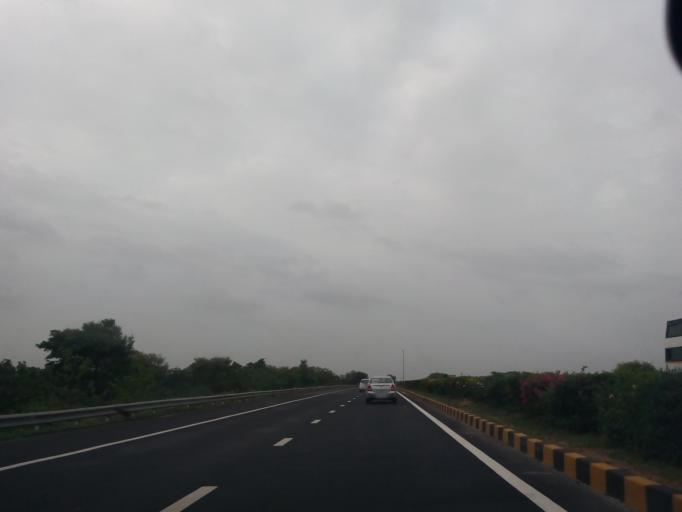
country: IN
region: Gujarat
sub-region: Kheda
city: Nadiad
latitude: 22.7434
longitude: 72.8629
